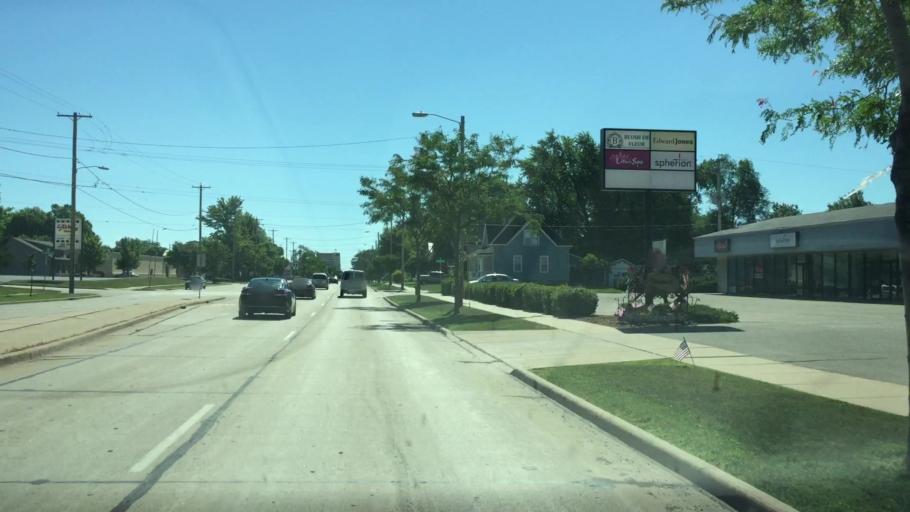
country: US
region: Wisconsin
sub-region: Outagamie County
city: Appleton
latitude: 44.2617
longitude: -88.4318
